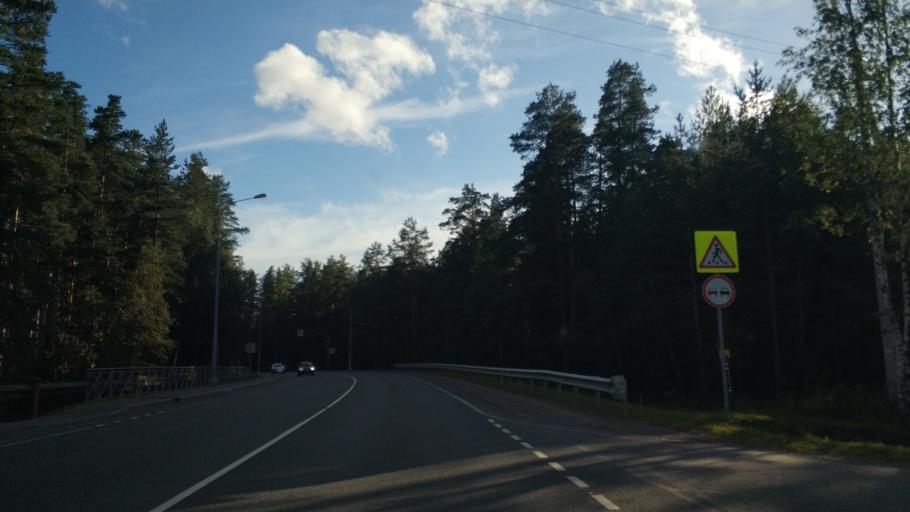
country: RU
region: Leningrad
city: Sapernoye
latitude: 60.7084
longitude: 29.9697
